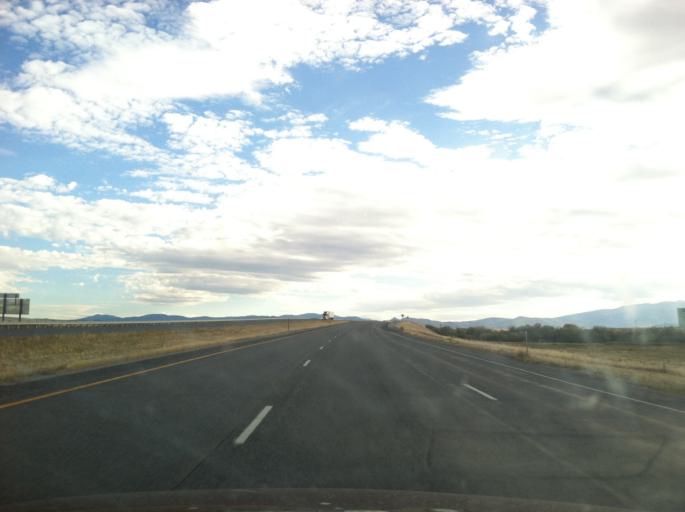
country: US
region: Montana
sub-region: Deer Lodge County
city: Warm Springs
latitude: 46.2680
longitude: -112.7495
